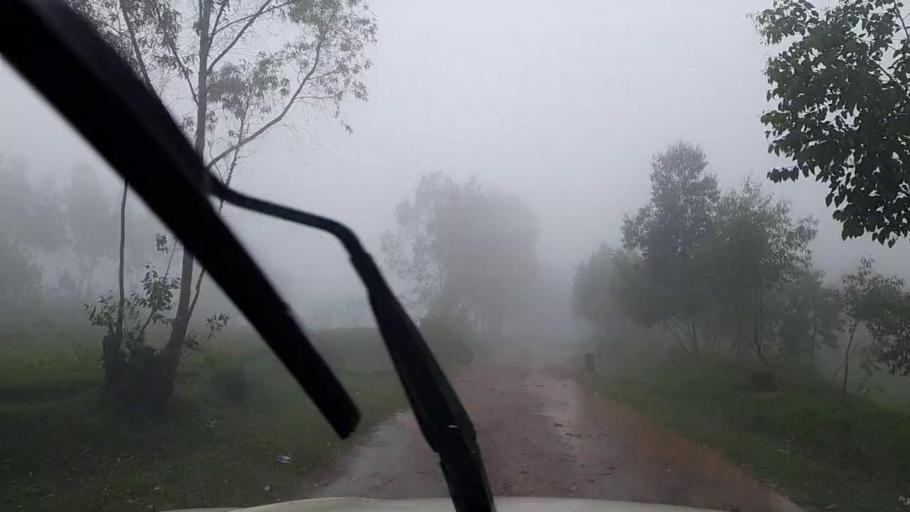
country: RW
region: Kigali
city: Kigali
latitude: -1.7703
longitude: 29.9977
